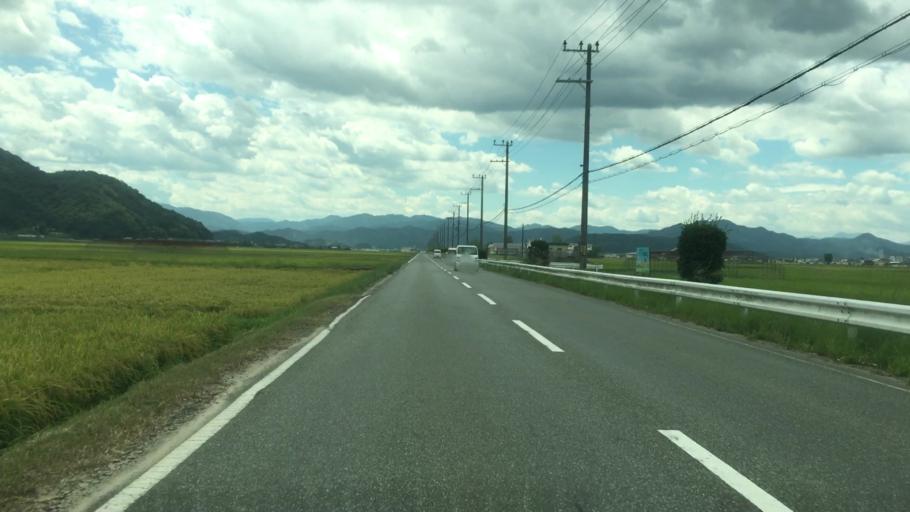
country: JP
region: Hyogo
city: Toyooka
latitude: 35.5388
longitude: 134.8396
